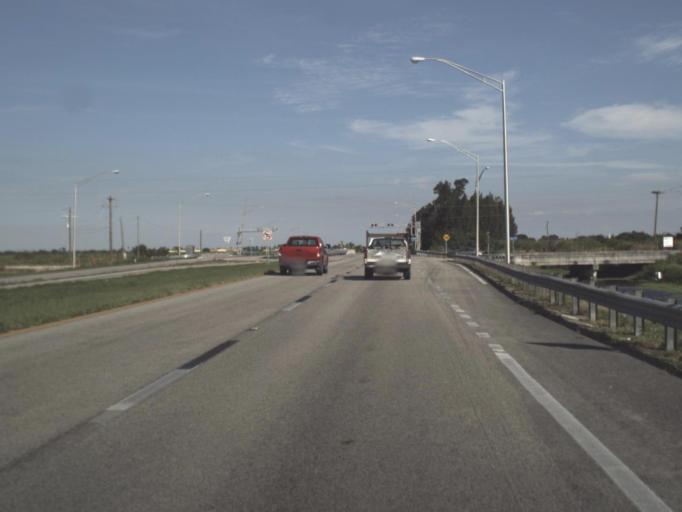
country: US
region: Florida
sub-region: Hendry County
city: Harlem
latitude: 26.7540
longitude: -80.9615
